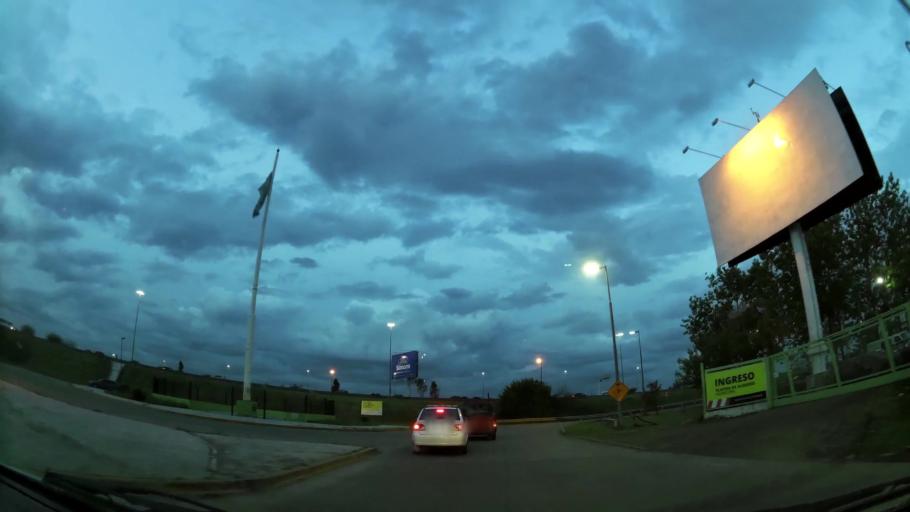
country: AR
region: Buenos Aires
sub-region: Partido de Quilmes
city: Quilmes
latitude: -34.7189
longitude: -58.2337
